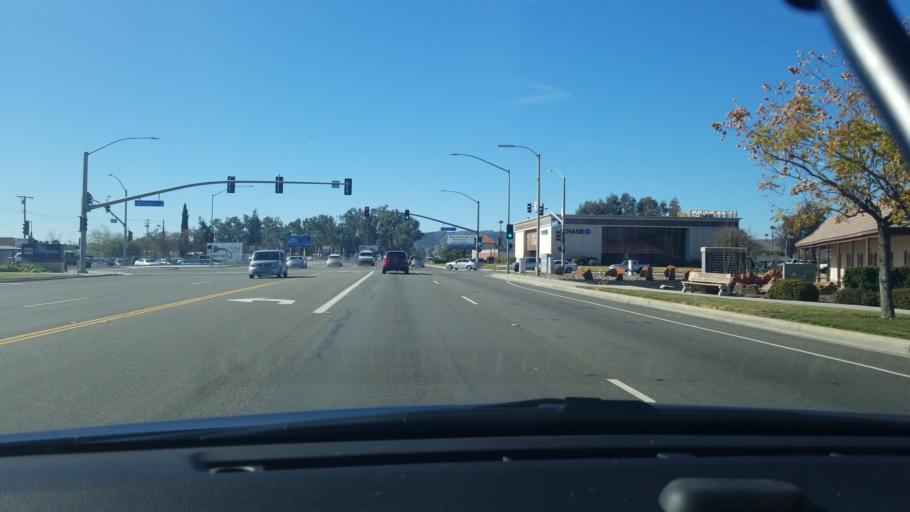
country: US
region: California
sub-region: Riverside County
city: Hemet
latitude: 33.7455
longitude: -117.0145
